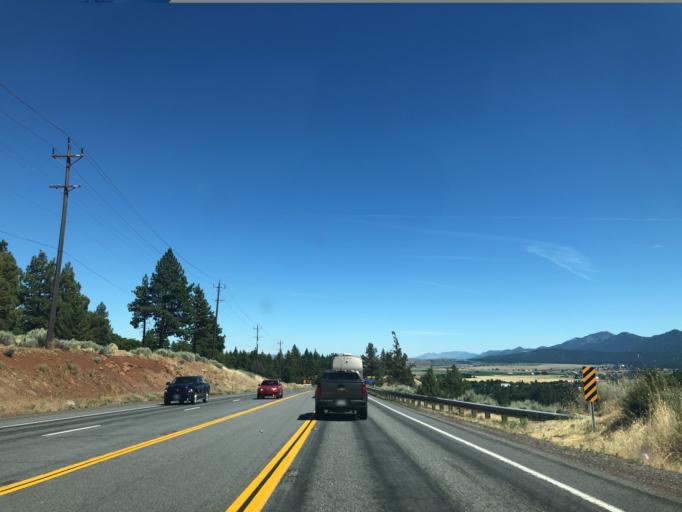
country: US
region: California
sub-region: Lassen County
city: Susanville
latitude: 40.4227
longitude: -120.6759
